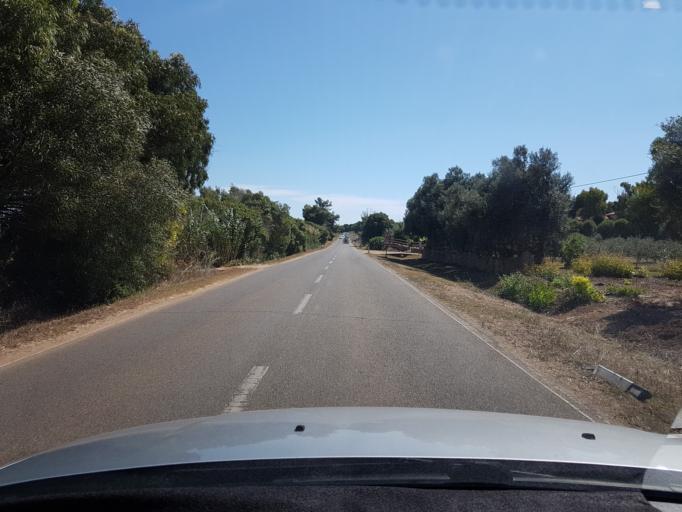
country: IT
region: Sardinia
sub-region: Provincia di Oristano
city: Cabras
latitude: 39.9035
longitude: 8.4366
